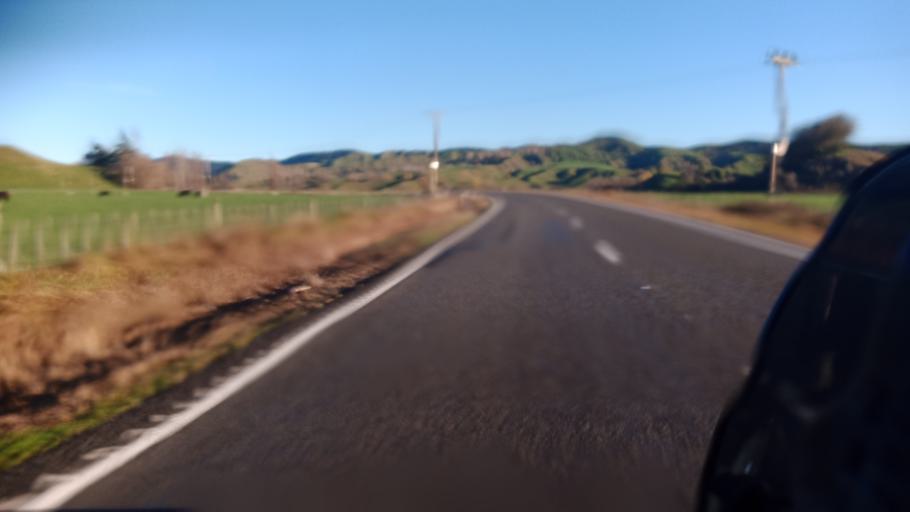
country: NZ
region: Hawke's Bay
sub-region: Wairoa District
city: Wairoa
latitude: -39.0179
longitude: 177.3707
